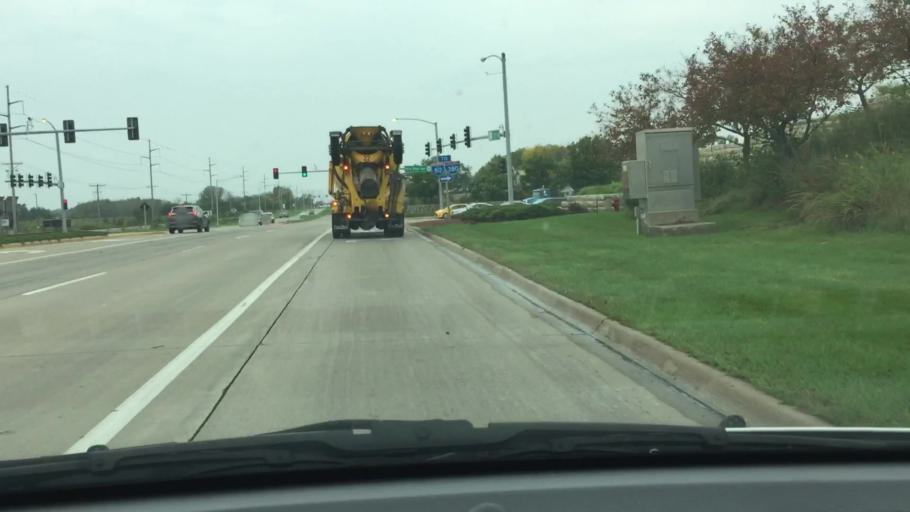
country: US
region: Iowa
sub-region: Johnson County
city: Coralville
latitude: 41.6882
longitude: -91.6080
